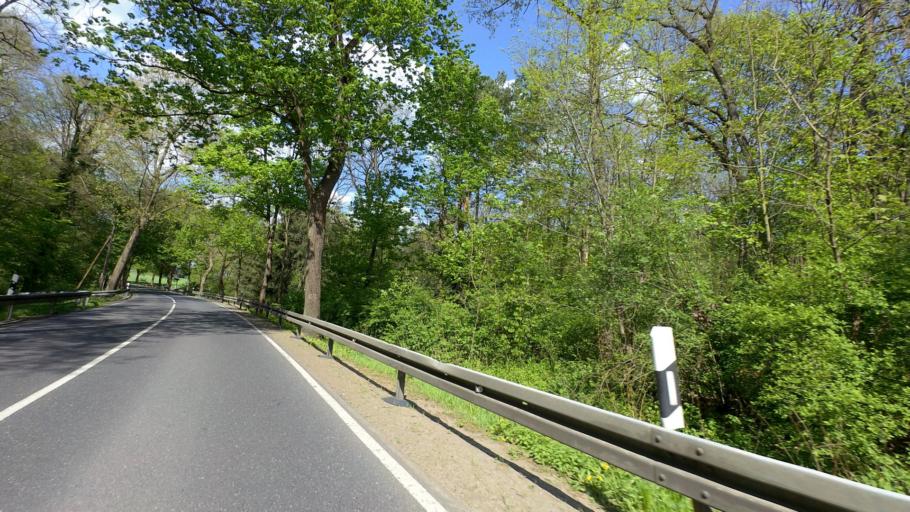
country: DE
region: Brandenburg
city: Marienwerder
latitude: 52.8872
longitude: 13.5456
